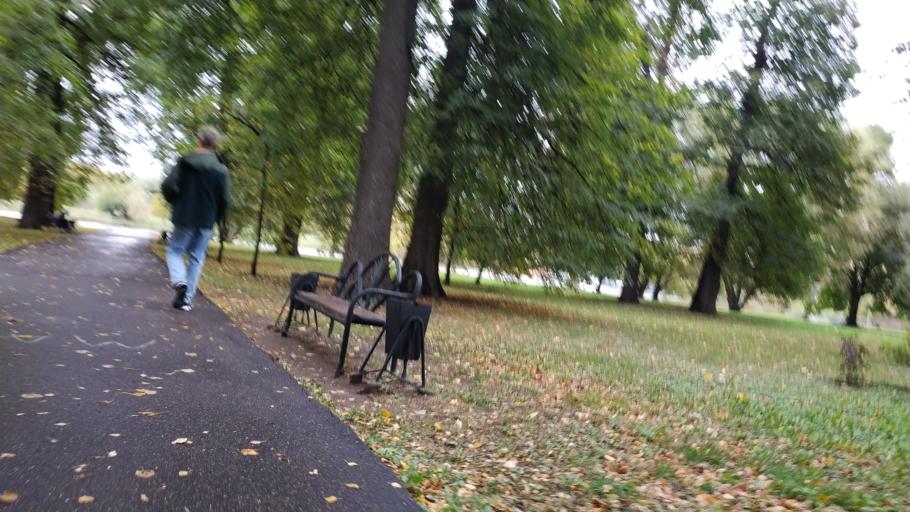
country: RU
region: Moscow
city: Metrogorodok
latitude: 55.7928
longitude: 37.7653
